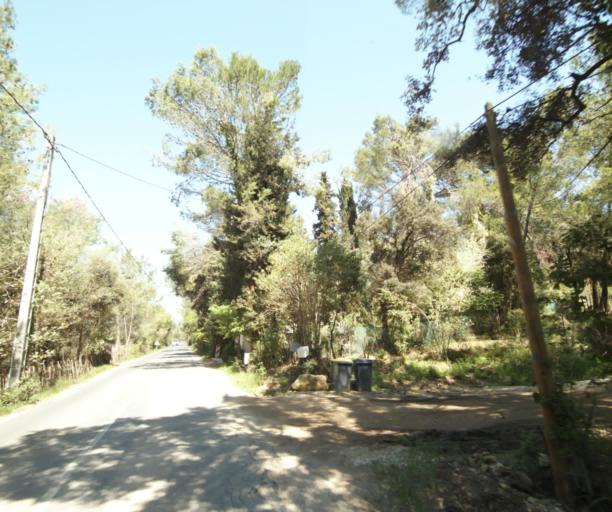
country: FR
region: Languedoc-Roussillon
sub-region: Departement de l'Herault
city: Saint-Genies-des-Mourgues
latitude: 43.6904
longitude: 4.0154
